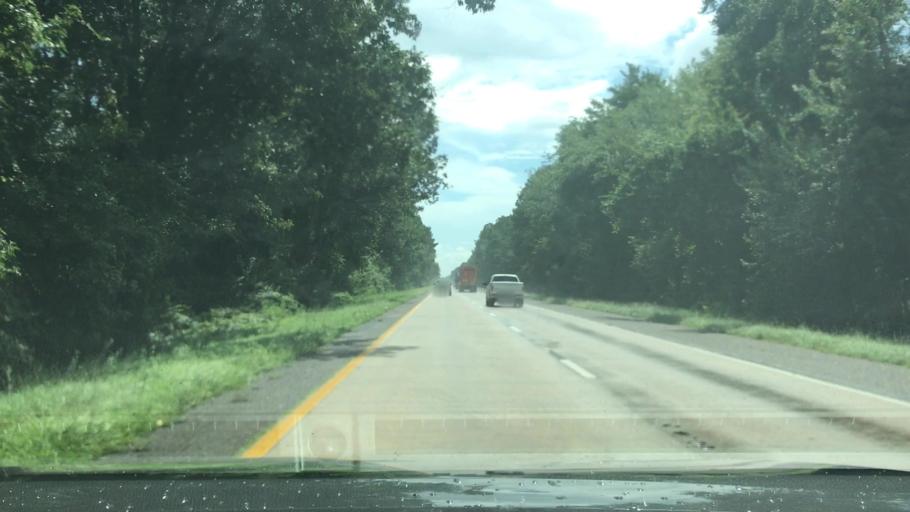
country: US
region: South Carolina
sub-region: Hampton County
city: Yemassee
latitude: 32.7771
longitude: -80.7957
